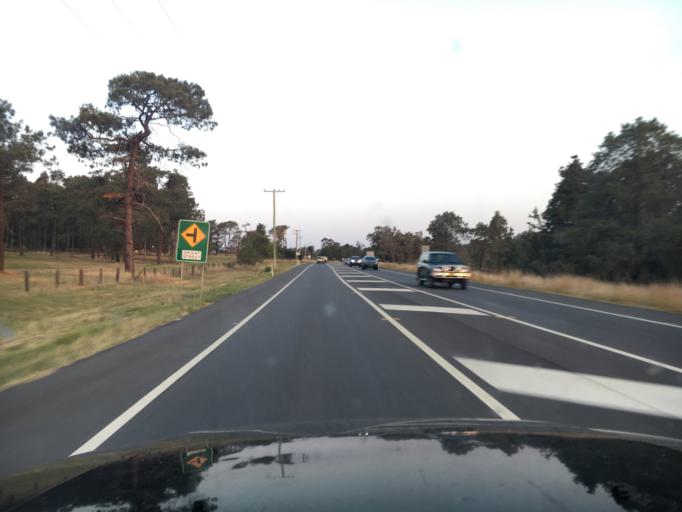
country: AU
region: New South Wales
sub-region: Cessnock
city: Greta
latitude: -32.6847
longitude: 151.3968
